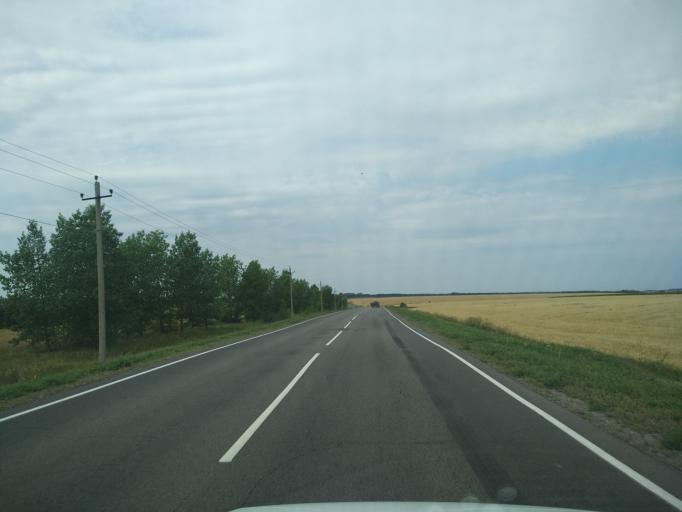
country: RU
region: Voronezj
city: Pereleshinskiy
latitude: 51.8236
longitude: 40.2753
